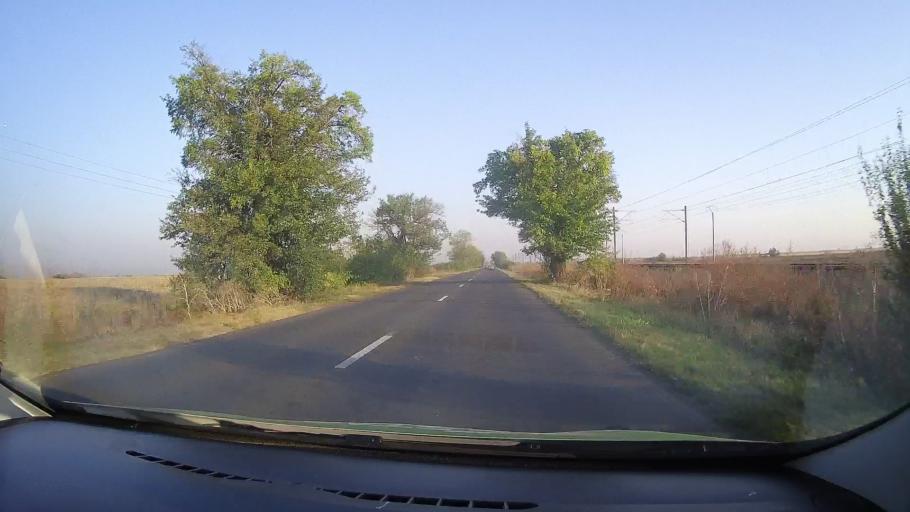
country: RO
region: Arad
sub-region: Comuna Sofronea
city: Sofronea
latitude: 46.2894
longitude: 21.3122
